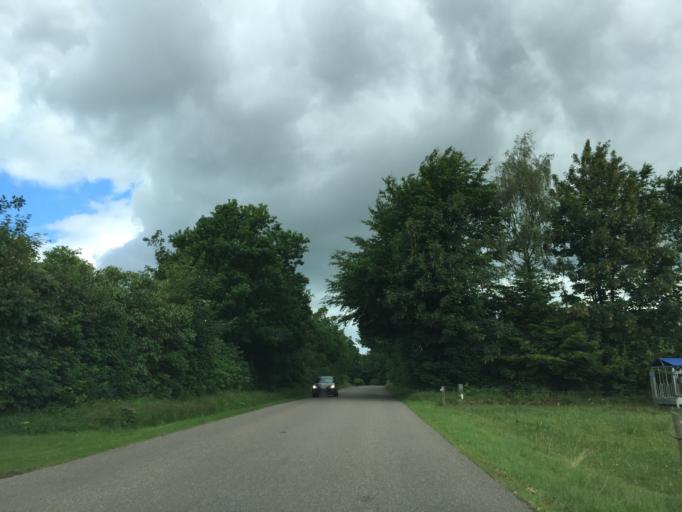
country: DK
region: Central Jutland
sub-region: Silkeborg Kommune
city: Svejbaek
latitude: 56.1702
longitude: 9.6541
